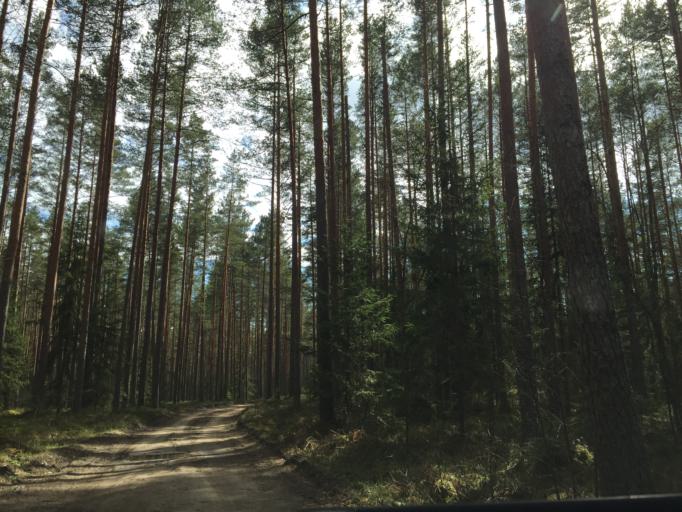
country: LV
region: Gulbenes Rajons
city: Gulbene
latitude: 57.2696
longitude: 26.5504
